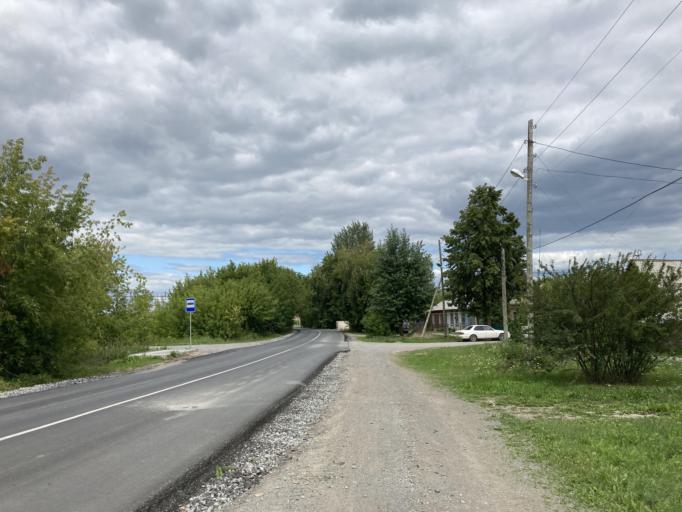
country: RU
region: Sverdlovsk
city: Bogdanovich
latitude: 56.7822
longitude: 62.0658
